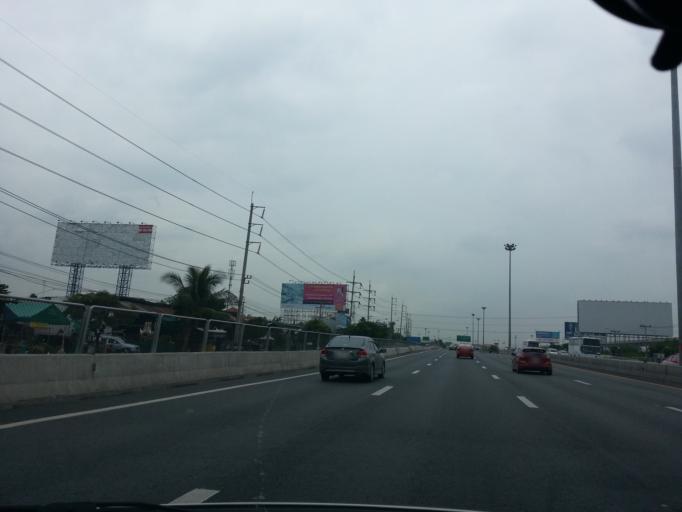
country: TH
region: Bangkok
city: Saphan Sung
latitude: 13.7337
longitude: 100.6932
